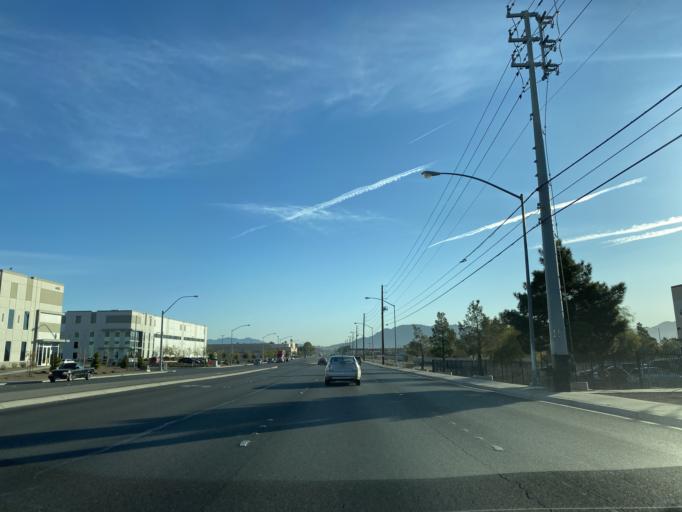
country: US
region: Nevada
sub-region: Clark County
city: Nellis Air Force Base
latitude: 36.2403
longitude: -115.0763
